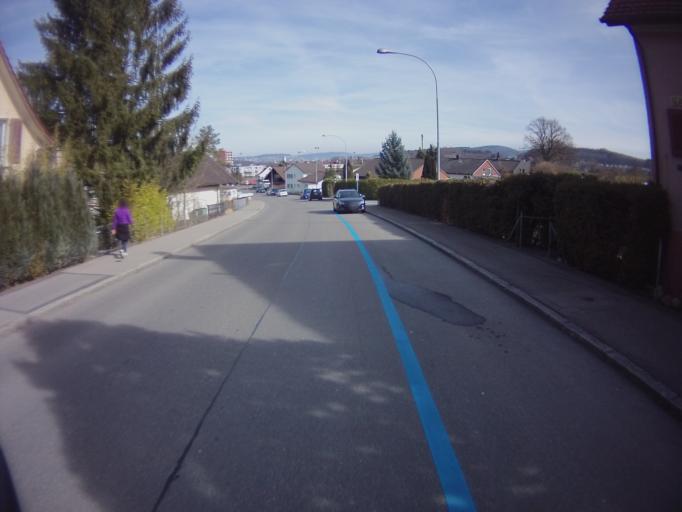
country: CH
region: Zurich
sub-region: Bezirk Dietikon
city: Dietikon / Almend
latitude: 47.4005
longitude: 8.3890
